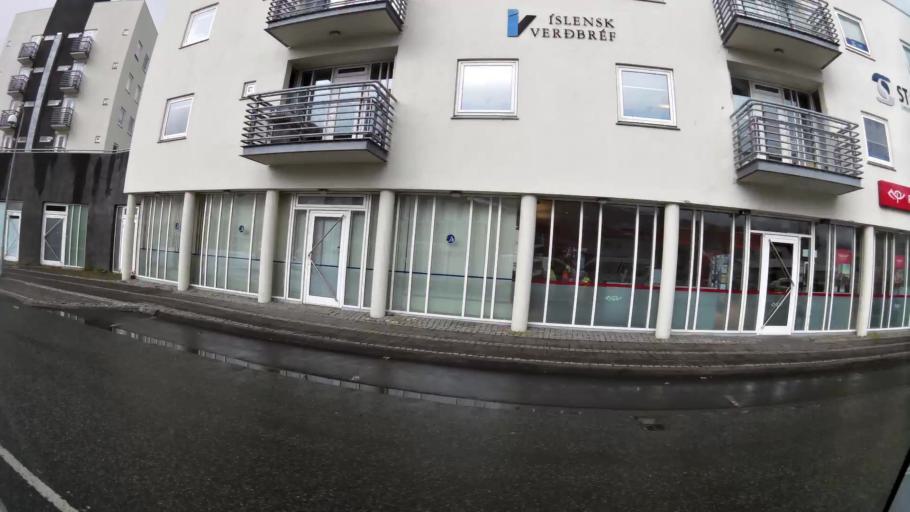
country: IS
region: Northeast
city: Akureyri
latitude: 65.6834
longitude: -18.0910
